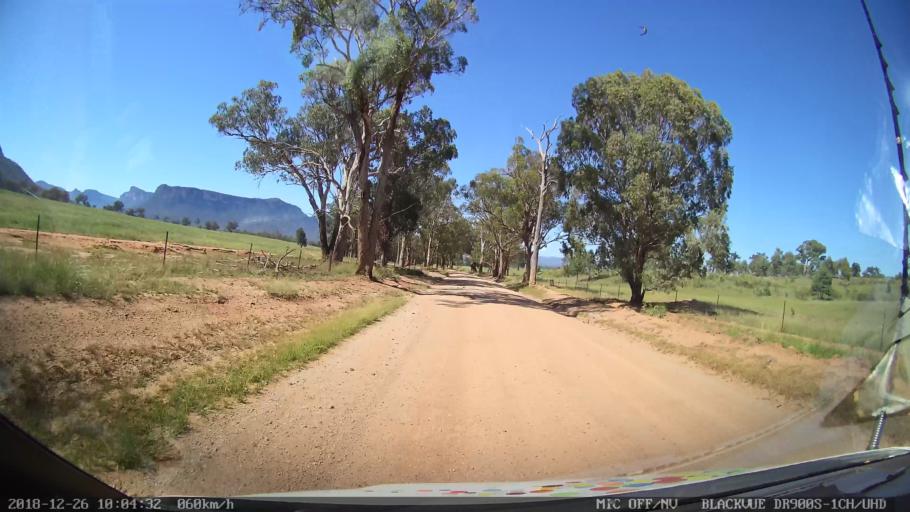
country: AU
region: New South Wales
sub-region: Mid-Western Regional
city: Kandos
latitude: -33.0710
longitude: 150.2138
